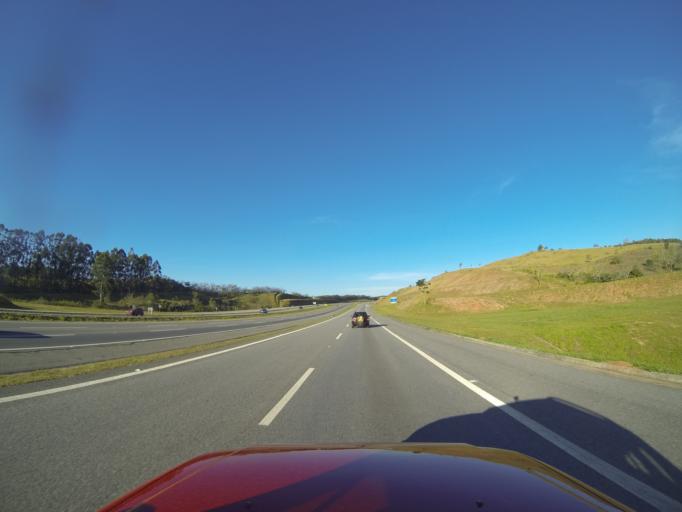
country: BR
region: Sao Paulo
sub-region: Jacarei
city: Jacarei
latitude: -23.3452
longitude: -46.0190
